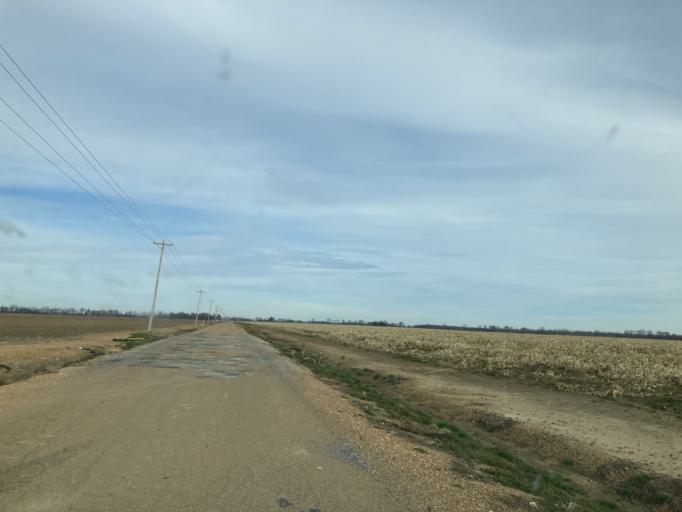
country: US
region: Mississippi
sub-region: Humphreys County
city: Belzoni
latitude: 33.0948
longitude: -90.6138
